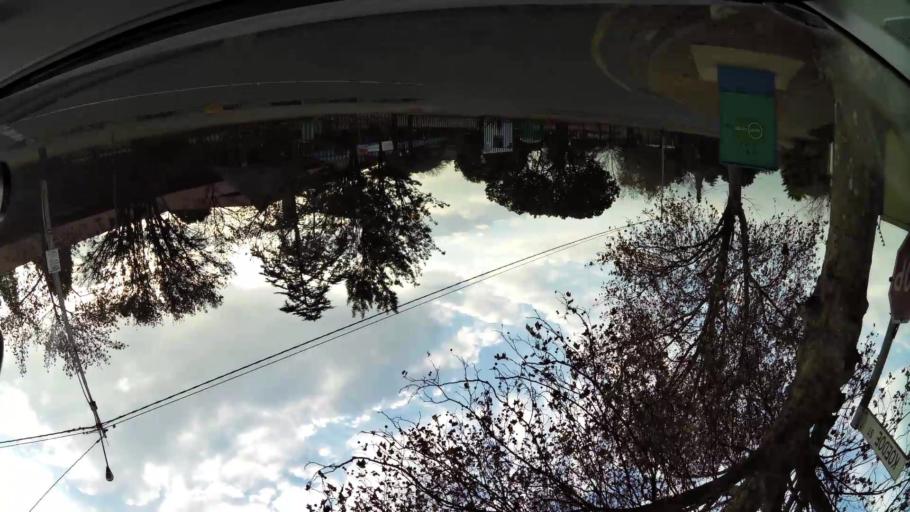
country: ZA
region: Gauteng
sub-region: Ekurhuleni Metropolitan Municipality
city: Germiston
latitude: -26.1730
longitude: 28.1727
